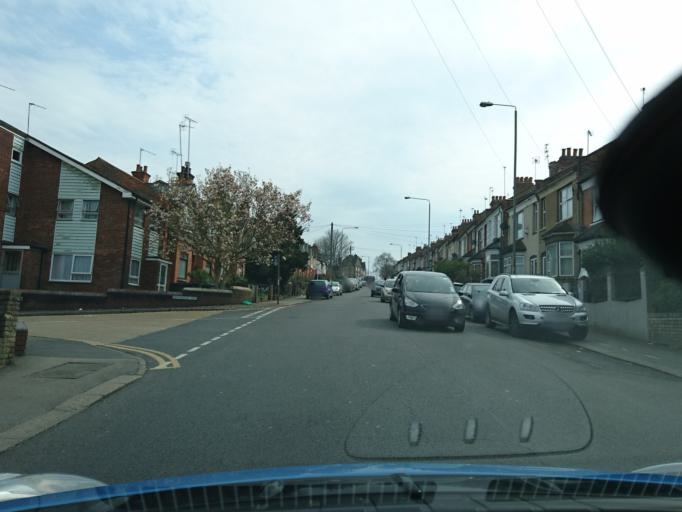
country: GB
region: England
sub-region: Greater London
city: Wood Green
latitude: 51.6193
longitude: -0.1425
